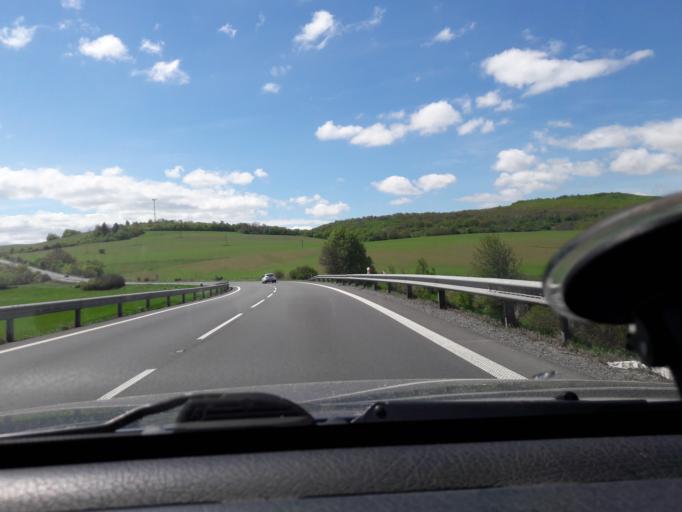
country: SK
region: Banskobystricky
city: Krupina
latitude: 48.4598
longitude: 19.0974
